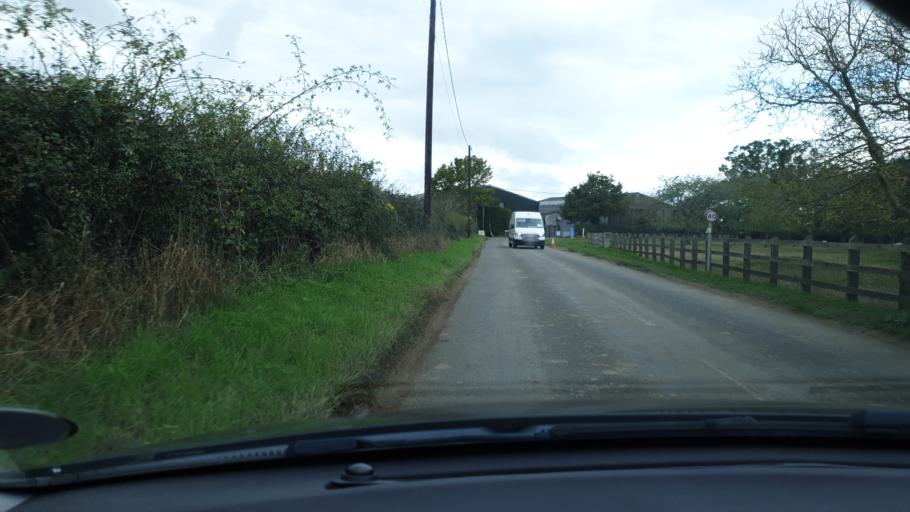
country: GB
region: England
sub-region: Essex
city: Mistley
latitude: 51.9324
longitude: 1.0955
